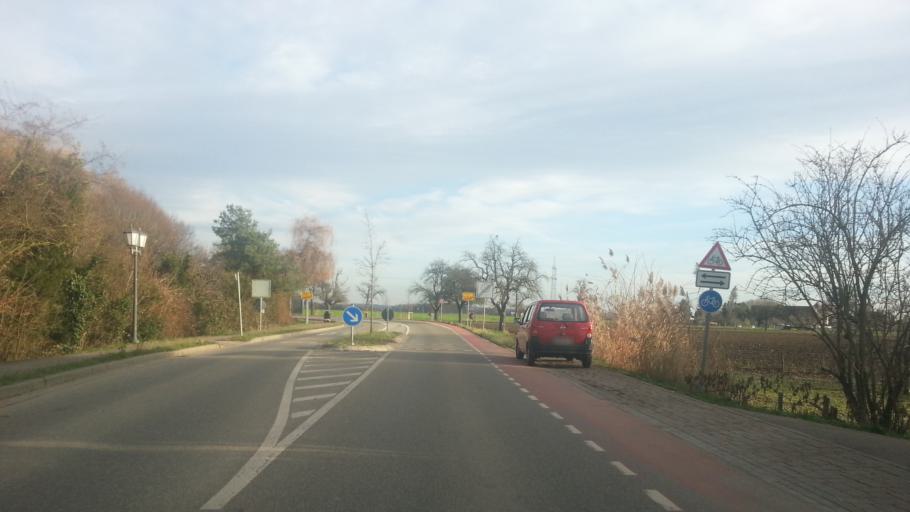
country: DE
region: Baden-Wuerttemberg
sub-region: Karlsruhe Region
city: Reilingen
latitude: 49.2946
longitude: 8.5793
